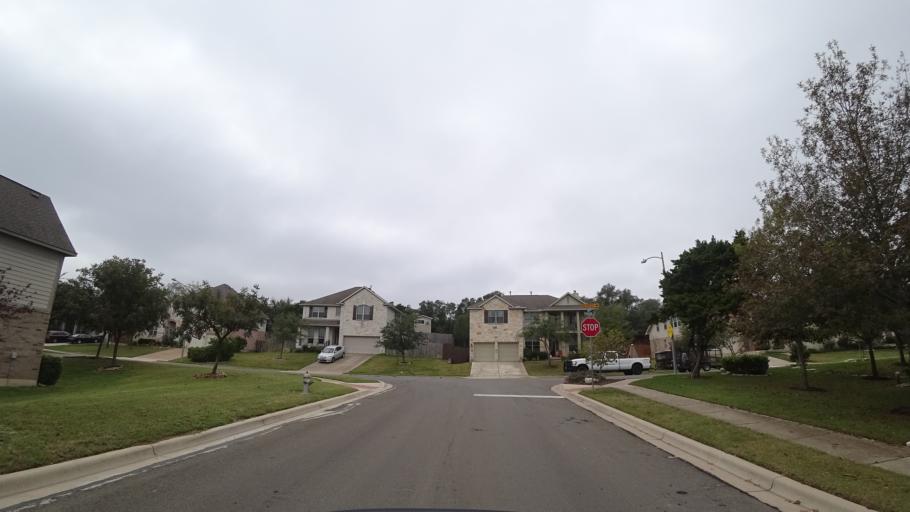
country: US
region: Texas
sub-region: Travis County
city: Barton Creek
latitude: 30.2385
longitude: -97.9042
